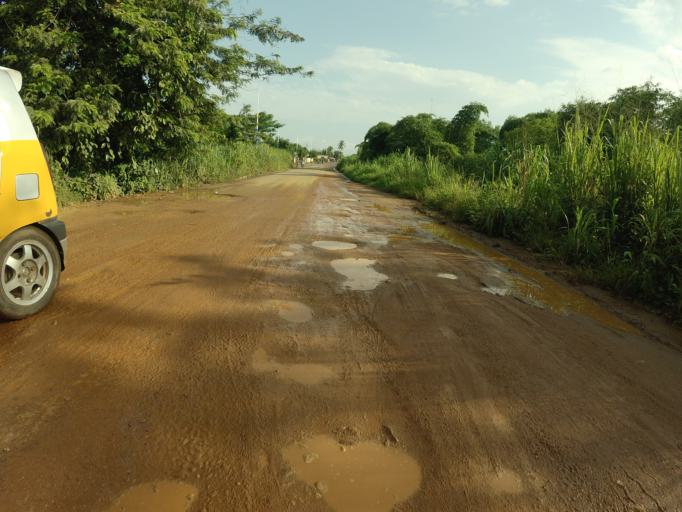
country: GH
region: Volta
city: Hohoe
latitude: 7.1181
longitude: 0.4575
